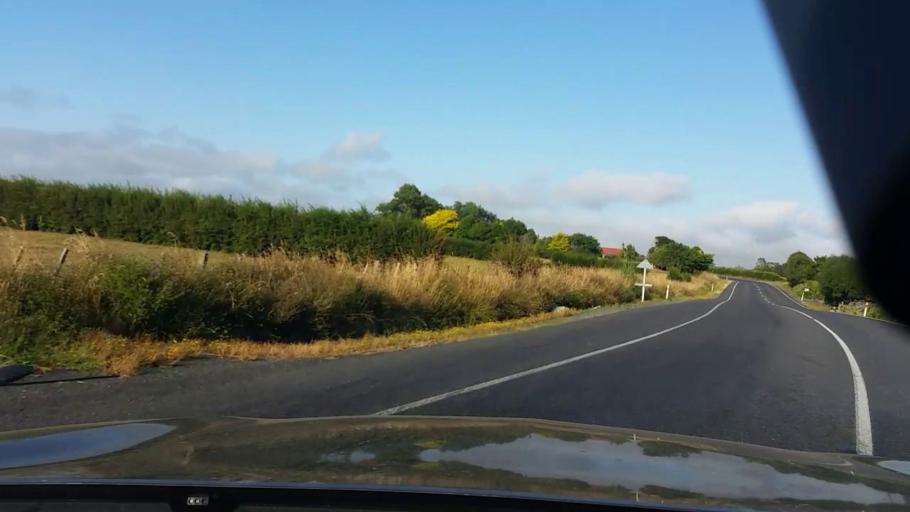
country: NZ
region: Waikato
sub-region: Hamilton City
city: Hamilton
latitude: -37.5889
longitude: 175.3907
